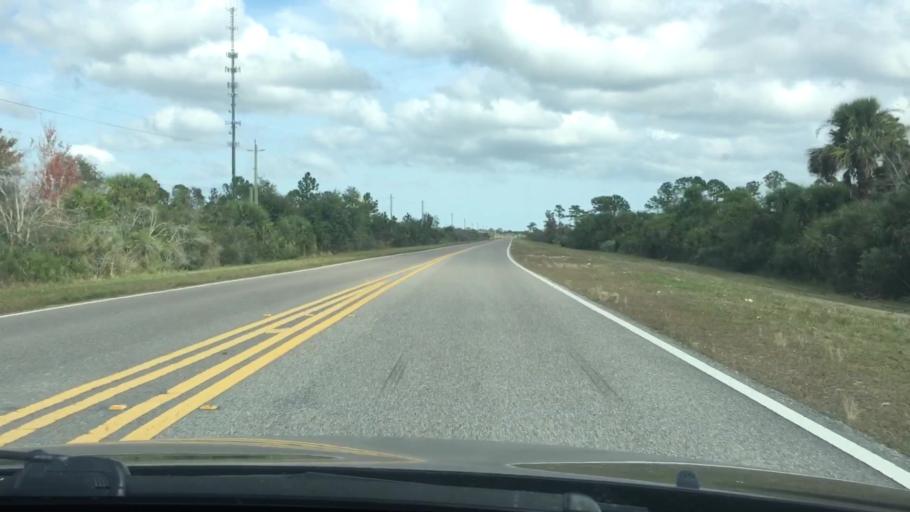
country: US
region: Florida
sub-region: Volusia County
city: Oak Hill
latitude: 28.7742
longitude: -80.8904
